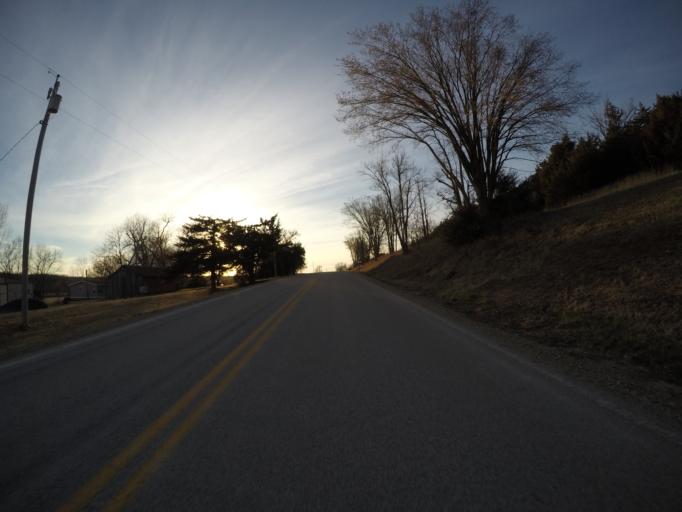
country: US
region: Kansas
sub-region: Riley County
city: Manhattan
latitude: 39.3057
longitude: -96.7242
